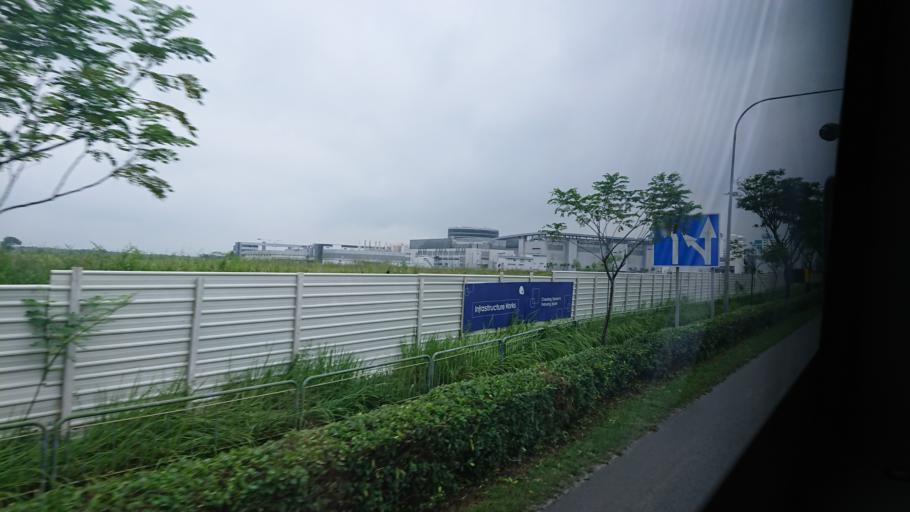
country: MY
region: Johor
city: Kampung Pasir Gudang Baru
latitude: 1.3780
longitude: 103.9265
